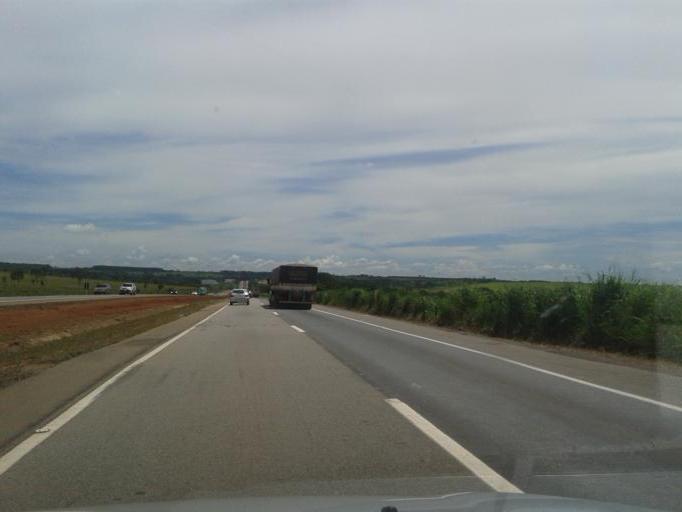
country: BR
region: Goias
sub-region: Hidrolandia
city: Hidrolandia
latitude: -17.0380
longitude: -49.2244
